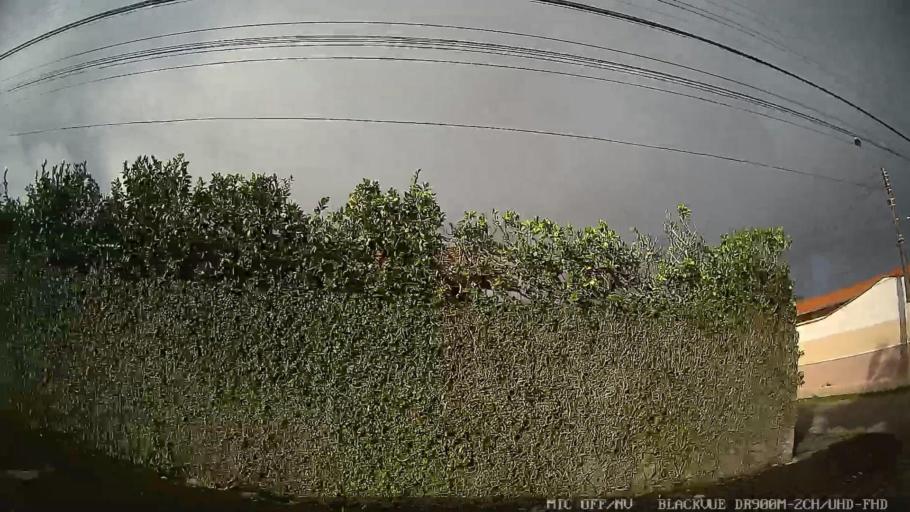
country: BR
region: Sao Paulo
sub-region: Itanhaem
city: Itanhaem
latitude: -24.1779
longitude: -46.7820
